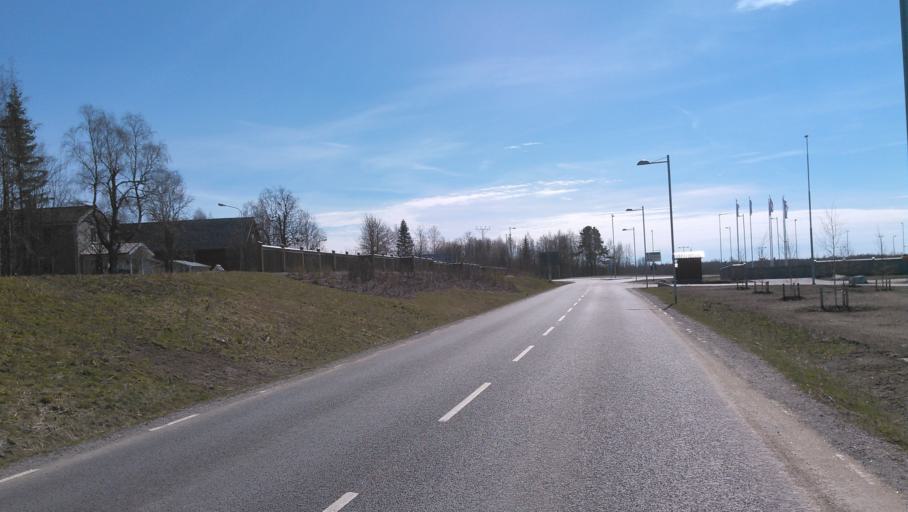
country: SE
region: Vaesterbotten
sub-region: Umea Kommun
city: Umea
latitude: 63.8063
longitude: 20.2574
